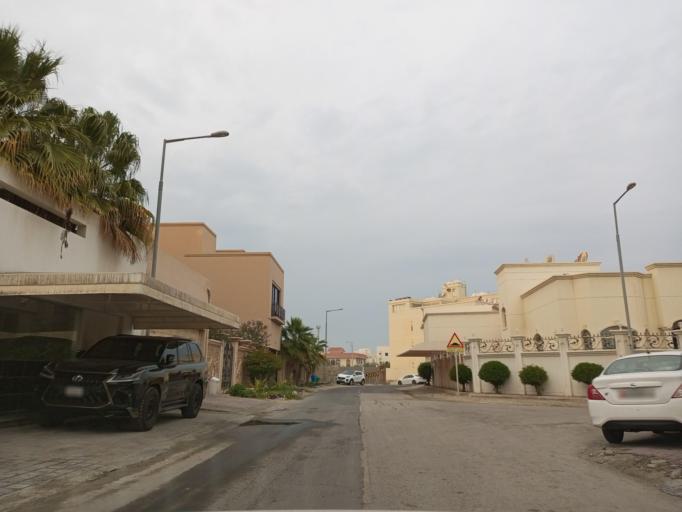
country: BH
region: Muharraq
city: Al Hadd
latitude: 26.2458
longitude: 50.6417
